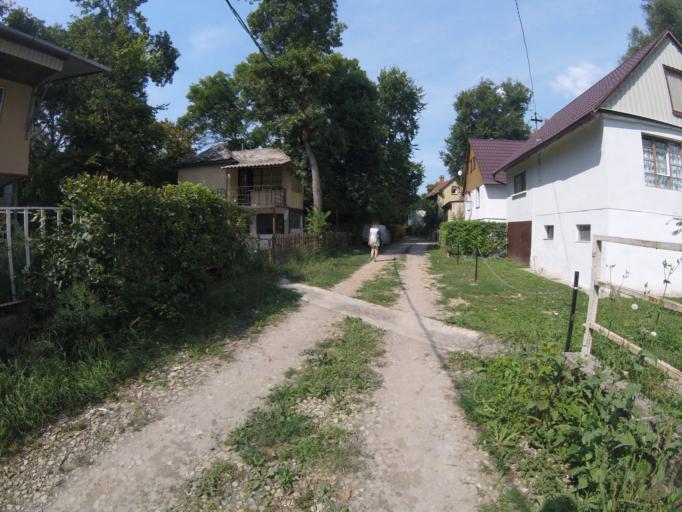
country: HU
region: Bacs-Kiskun
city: Baja
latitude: 46.1952
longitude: 18.9224
